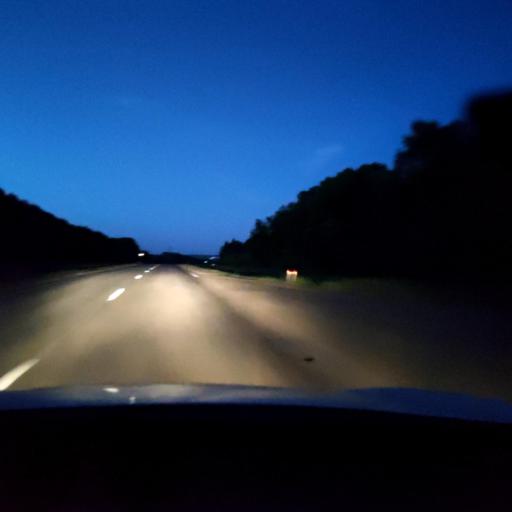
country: RU
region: Tatarstan
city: Rybnaya Sloboda
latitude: 55.4642
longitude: 49.9510
